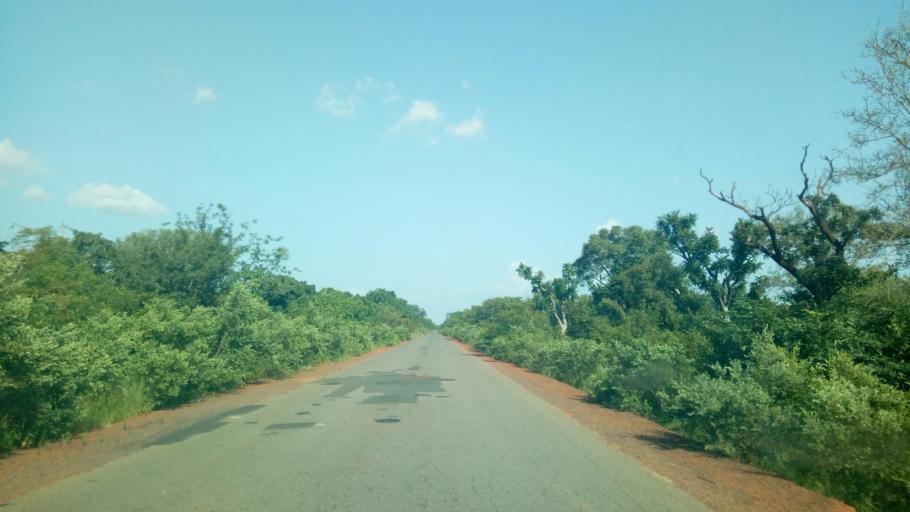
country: ML
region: Sikasso
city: Yorosso
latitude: 12.2111
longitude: -4.8896
